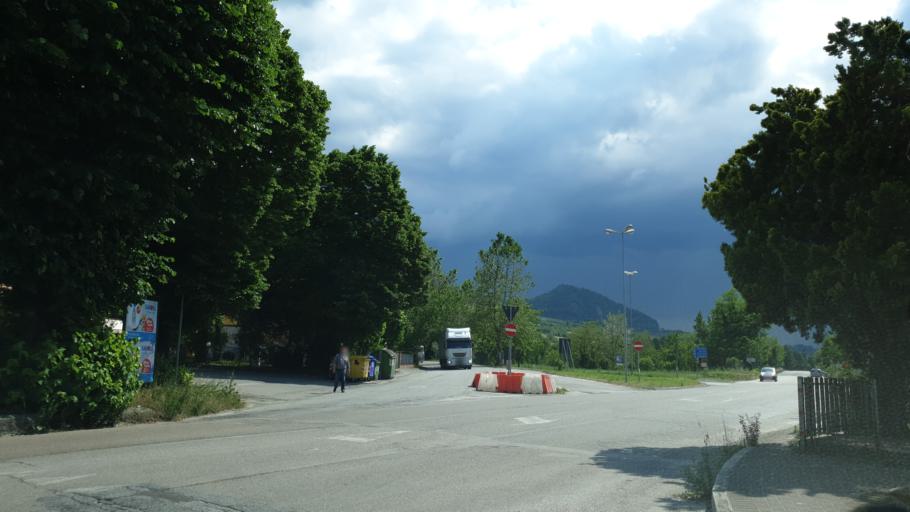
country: IT
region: Emilia-Romagna
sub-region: Provincia di Rimini
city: Pietracuta
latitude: 43.9520
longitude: 12.3686
